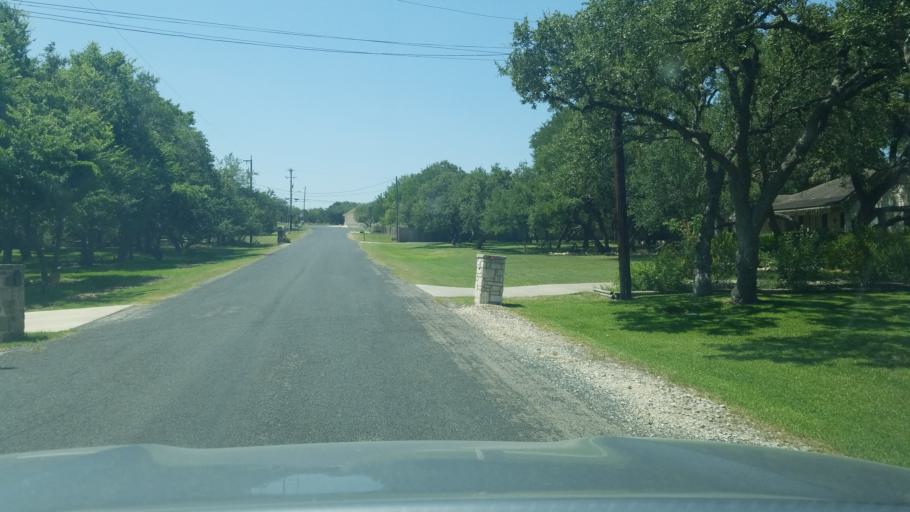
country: US
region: Texas
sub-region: Bexar County
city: Timberwood Park
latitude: 29.6970
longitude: -98.4876
